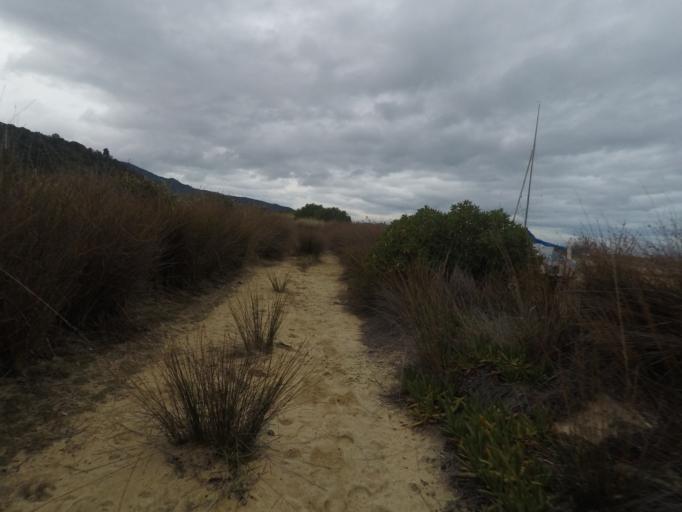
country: NZ
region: Tasman
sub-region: Tasman District
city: Motueka
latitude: -41.0122
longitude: 173.0069
